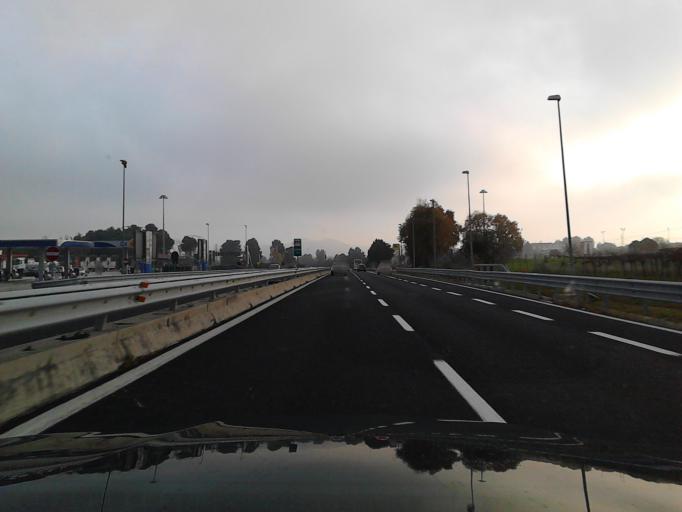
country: IT
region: Abruzzo
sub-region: Provincia di Chieti
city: Miglianico
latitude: 42.3893
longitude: 14.2886
